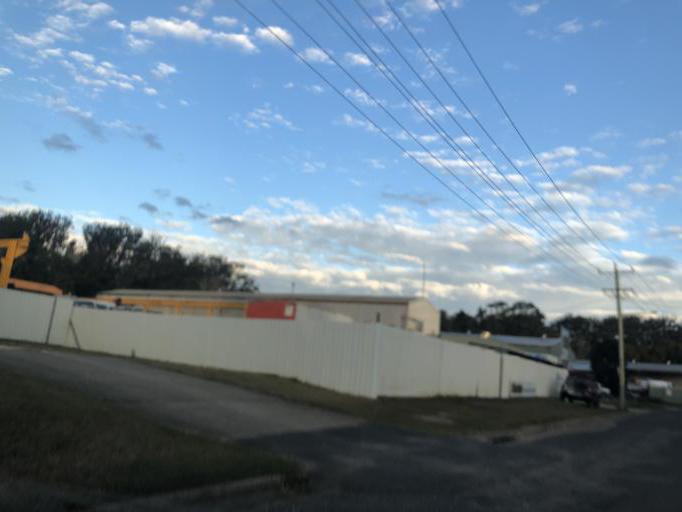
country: AU
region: New South Wales
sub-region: Nambucca Shire
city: Macksville
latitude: -30.7267
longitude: 152.9123
